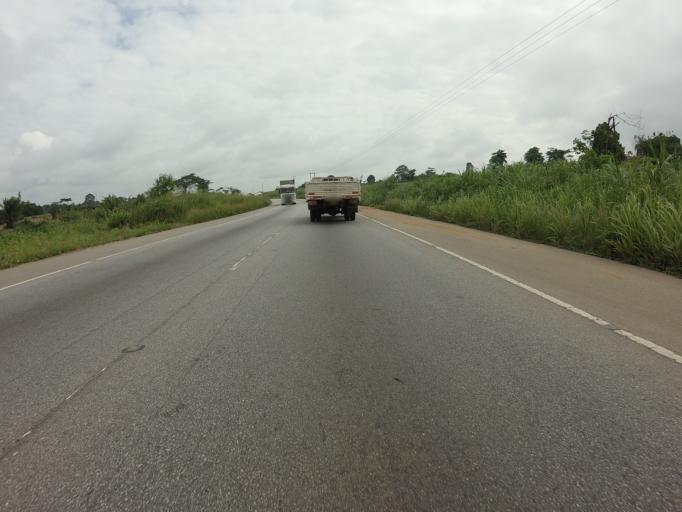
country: GH
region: Ashanti
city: Tafo
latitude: 6.9835
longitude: -1.6880
